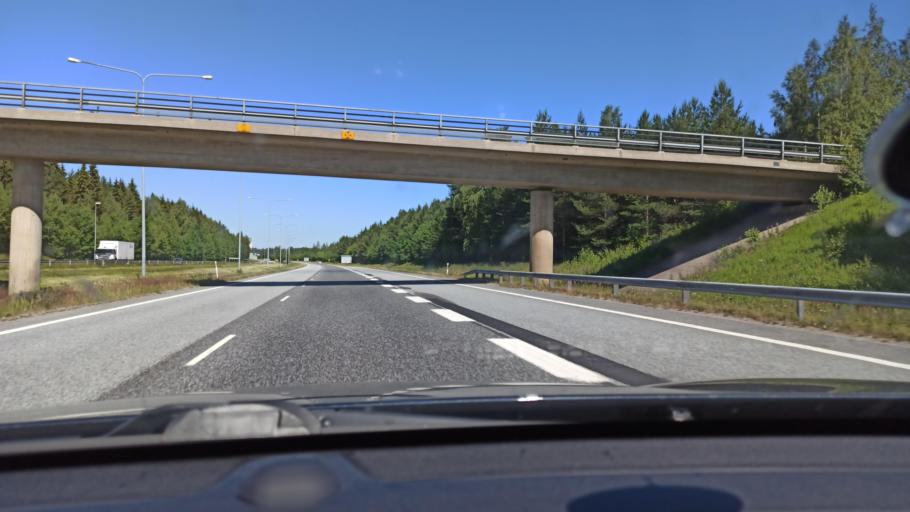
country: FI
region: Ostrobothnia
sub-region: Vaasa
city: Ristinummi
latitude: 63.0579
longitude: 21.7117
